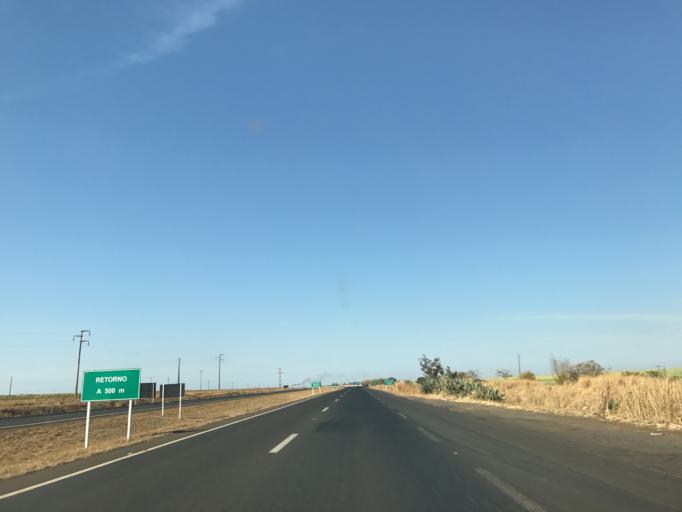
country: BR
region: Goias
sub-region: Morrinhos
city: Morrinhos
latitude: -17.8501
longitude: -49.2204
